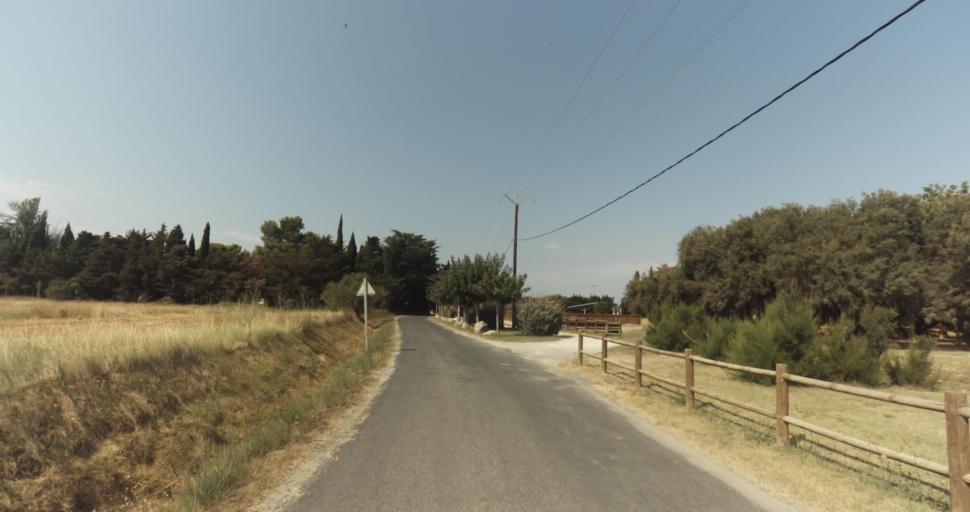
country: FR
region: Languedoc-Roussillon
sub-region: Departement des Pyrenees-Orientales
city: Latour-Bas-Elne
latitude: 42.6105
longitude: 3.0109
